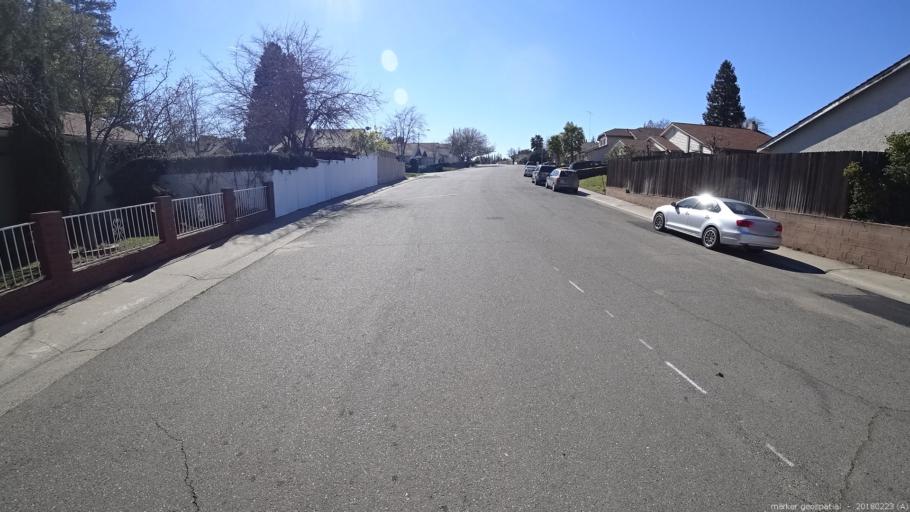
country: US
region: California
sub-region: Sacramento County
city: North Highlands
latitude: 38.7077
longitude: -121.3769
